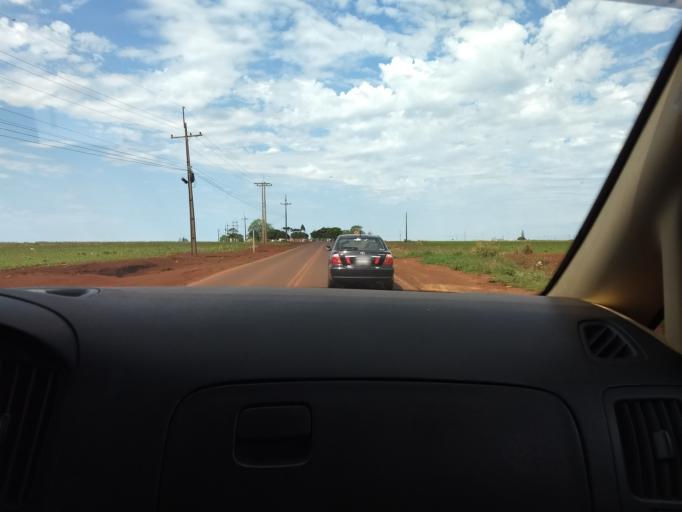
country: PY
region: Alto Parana
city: Santa Rita
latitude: -25.8021
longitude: -55.0667
